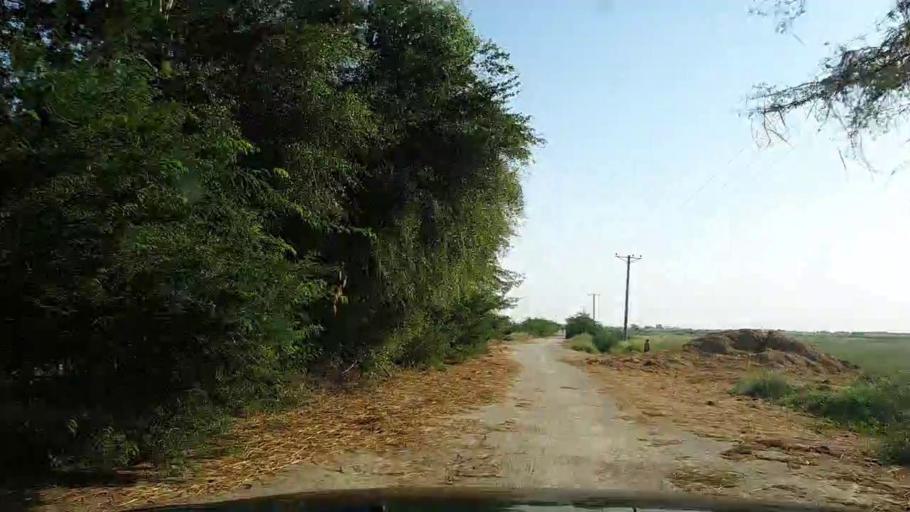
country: PK
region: Sindh
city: Thatta
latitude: 24.6449
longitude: 68.0751
